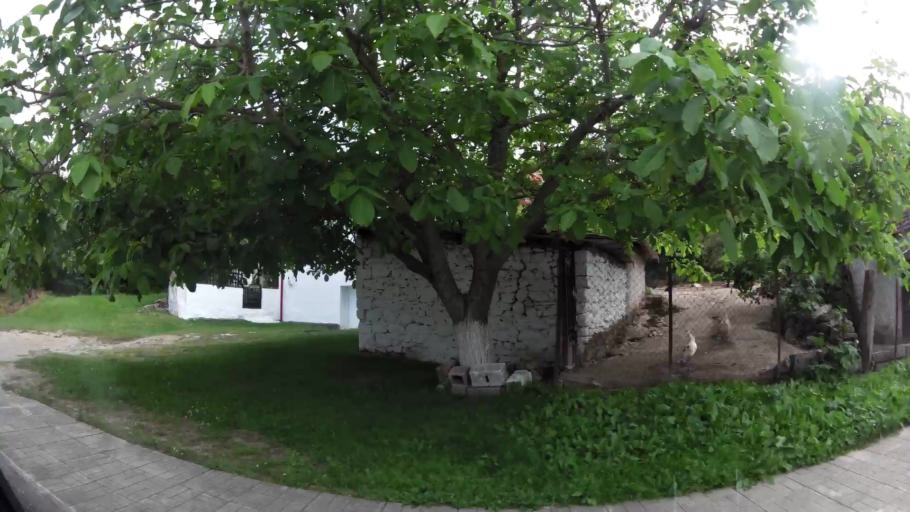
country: GR
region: West Macedonia
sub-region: Nomos Kozanis
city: Koila
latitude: 40.3478
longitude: 21.8391
